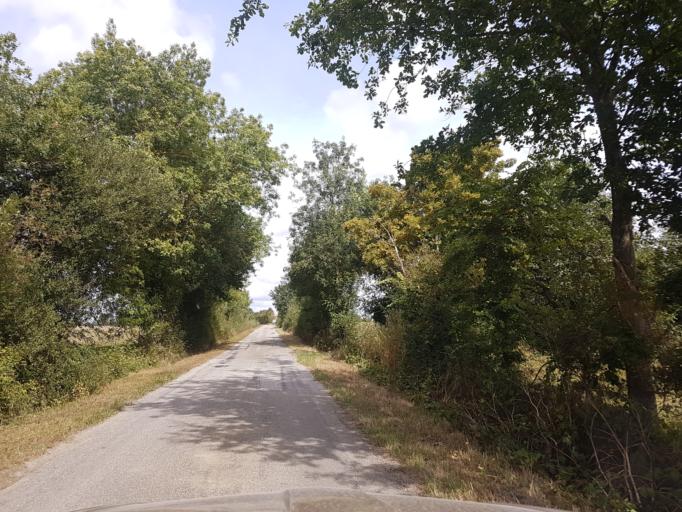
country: FR
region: Pays de la Loire
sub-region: Departement de la Loire-Atlantique
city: Petit-Mars
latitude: 47.4135
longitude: -1.4468
